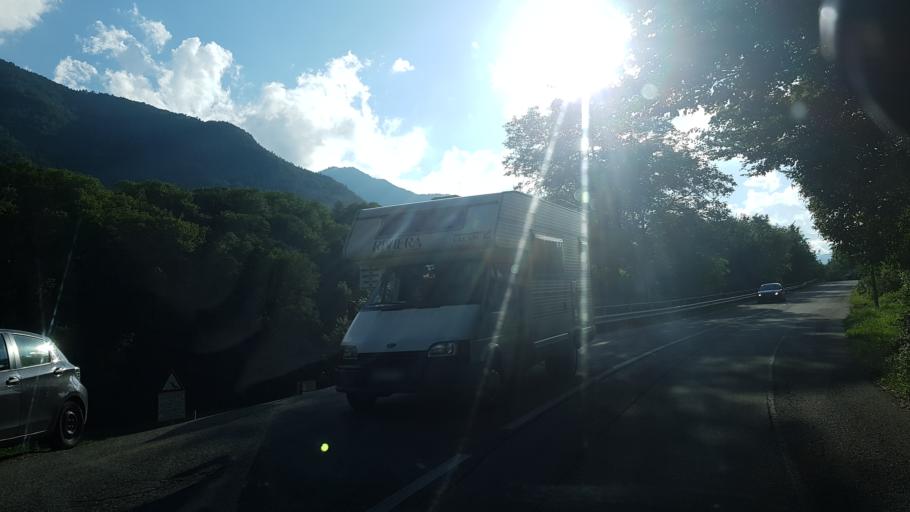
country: IT
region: Piedmont
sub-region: Provincia di Cuneo
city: Sampeyre
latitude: 44.5757
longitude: 7.1945
